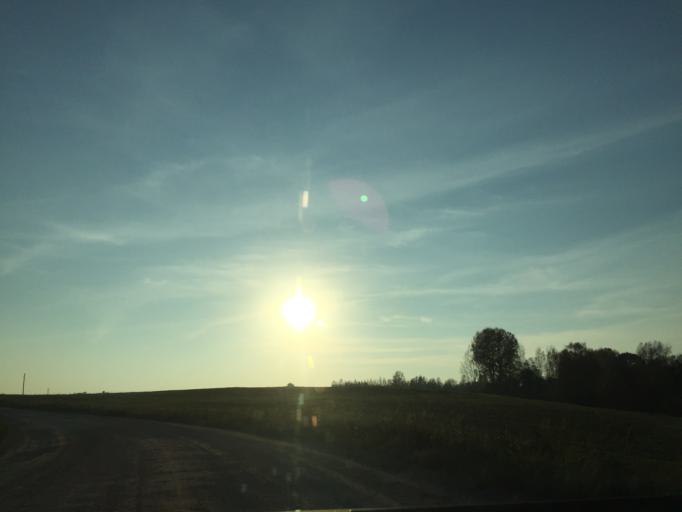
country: LV
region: Vainode
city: Vainode
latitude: 56.5615
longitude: 21.8451
